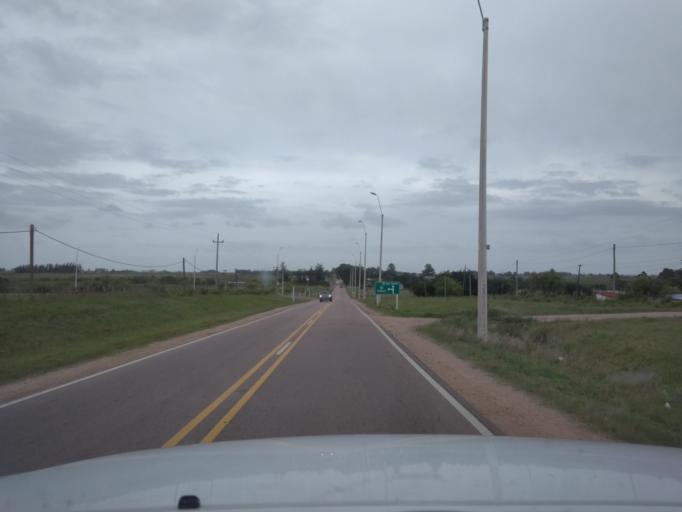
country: UY
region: Canelones
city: Tala
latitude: -34.3613
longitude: -55.7758
